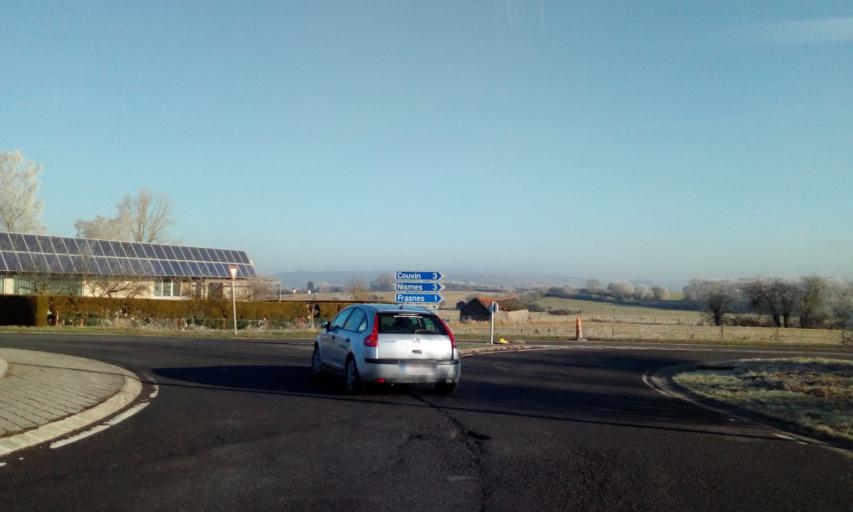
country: BE
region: Wallonia
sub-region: Province de Namur
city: Couvin
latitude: 50.0806
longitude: 4.5149
